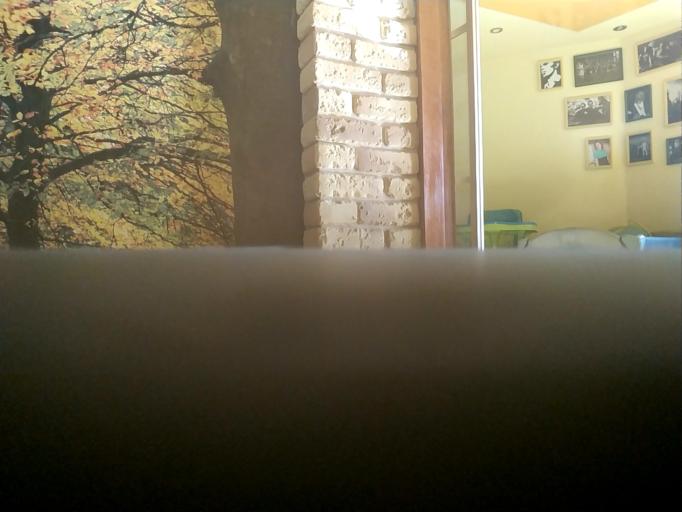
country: RU
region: Smolensk
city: Temkino
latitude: 54.9857
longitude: 34.9431
